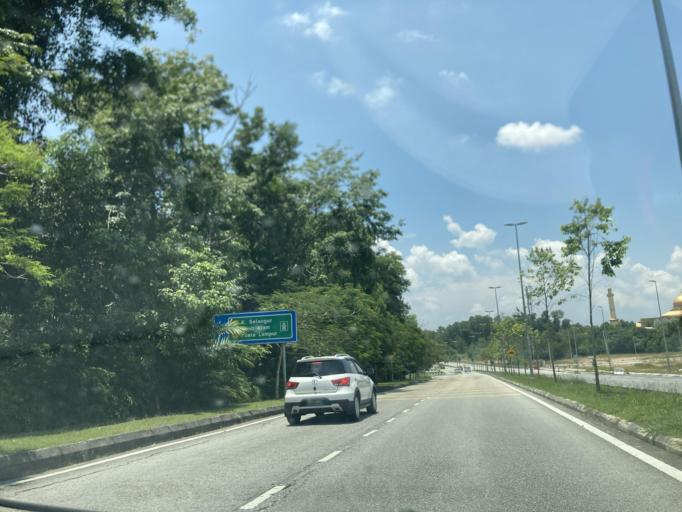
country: MY
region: Selangor
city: Batu Arang
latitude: 3.2908
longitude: 101.4779
